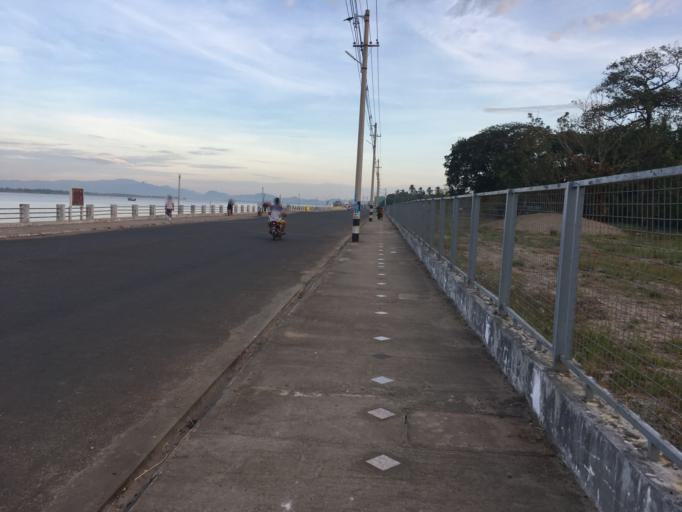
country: MM
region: Mon
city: Mawlamyine
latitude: 16.4594
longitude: 97.6233
